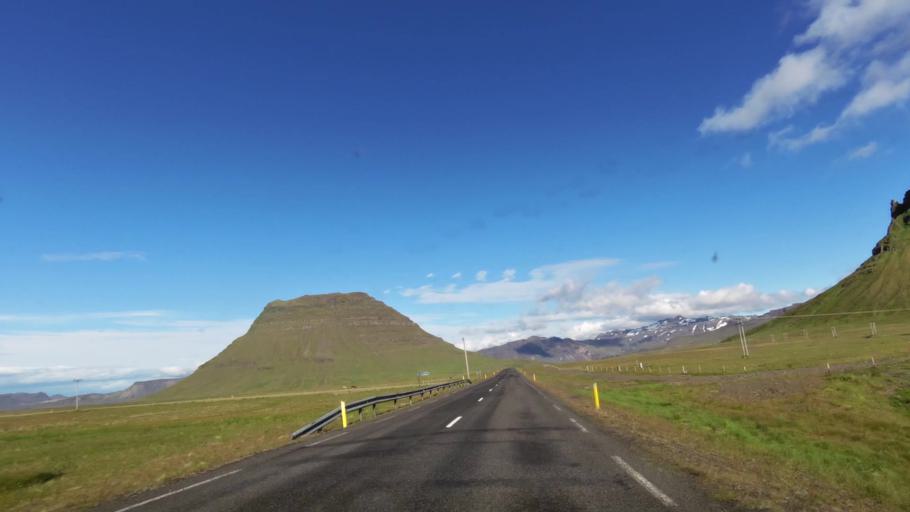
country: IS
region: West
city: Olafsvik
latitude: 64.9408
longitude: -23.3714
